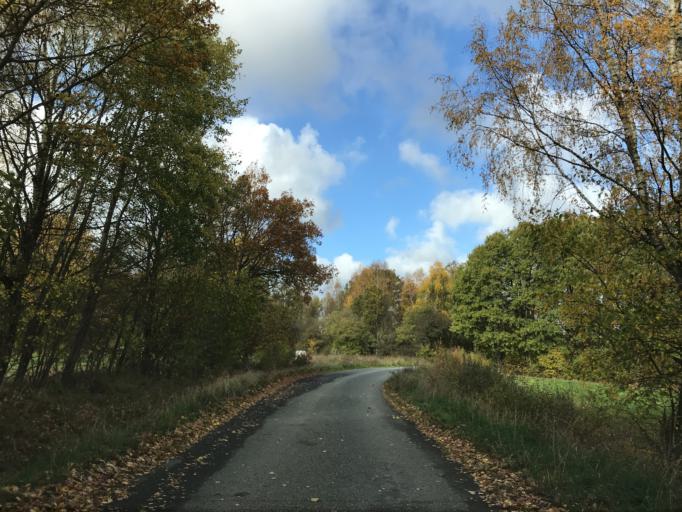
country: SE
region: Skane
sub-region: Perstorps Kommun
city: Perstorp
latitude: 56.0258
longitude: 13.3881
